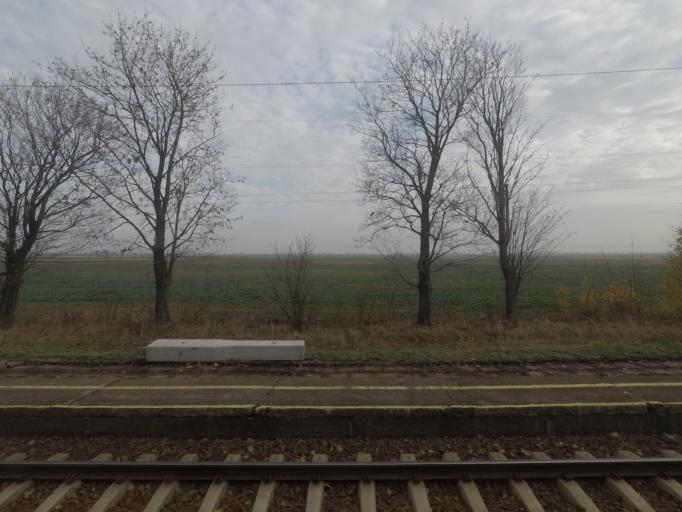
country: PL
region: Subcarpathian Voivodeship
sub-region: Powiat jaroslawski
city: Sosnica
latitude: 49.8593
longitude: 22.8553
